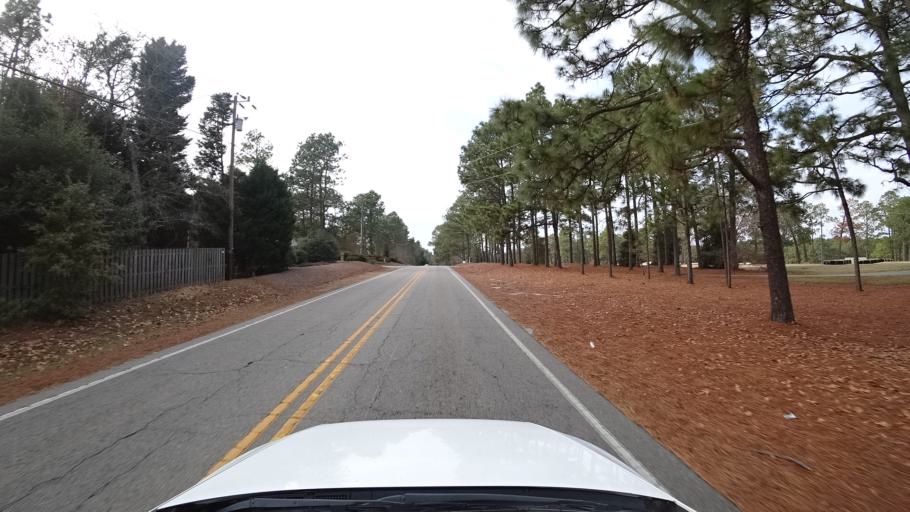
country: US
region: North Carolina
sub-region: Moore County
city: Pinehurst
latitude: 35.1823
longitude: -79.4578
